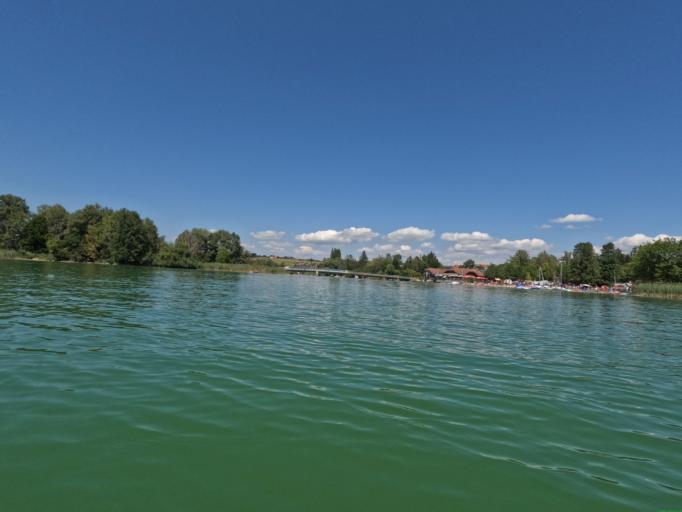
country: DE
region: Bavaria
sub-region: Upper Bavaria
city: Taching am See
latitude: 47.9520
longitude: 12.7495
